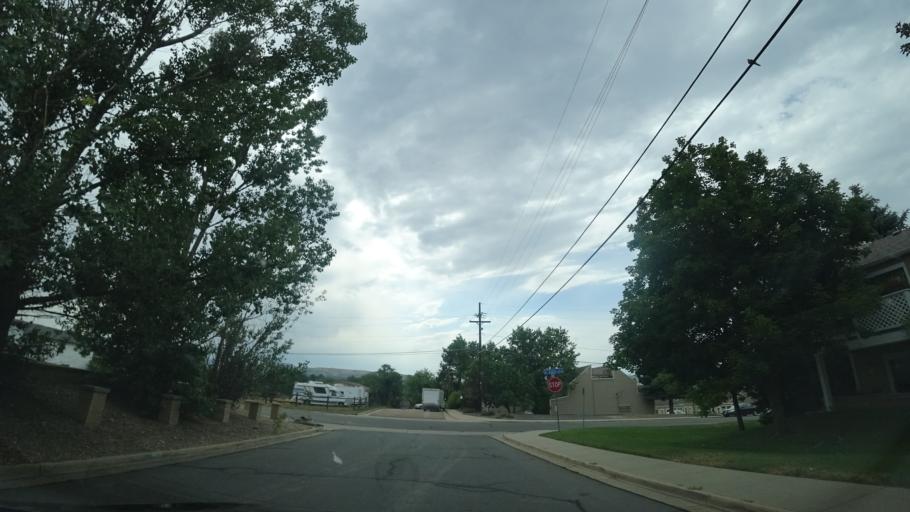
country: US
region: Colorado
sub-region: Jefferson County
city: Lakewood
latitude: 39.7093
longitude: -105.0951
